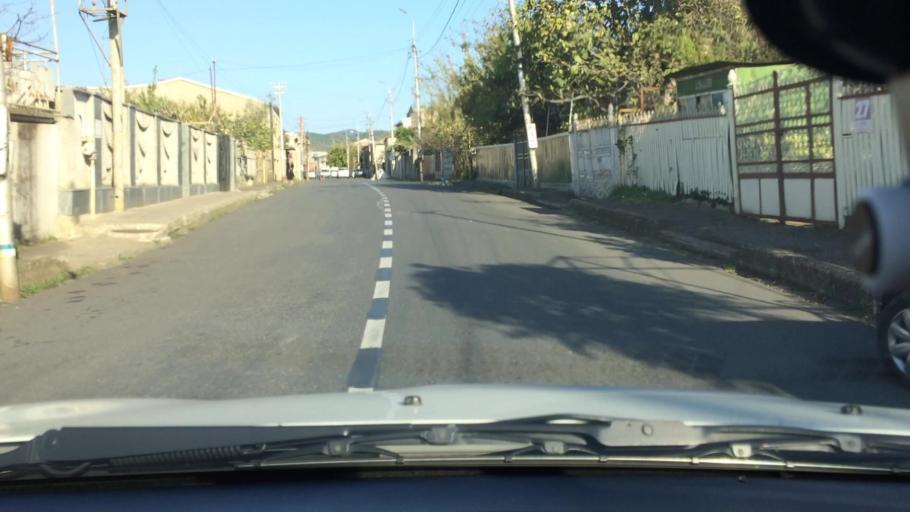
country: GE
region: Imereti
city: Kutaisi
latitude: 42.2706
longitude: 42.7136
